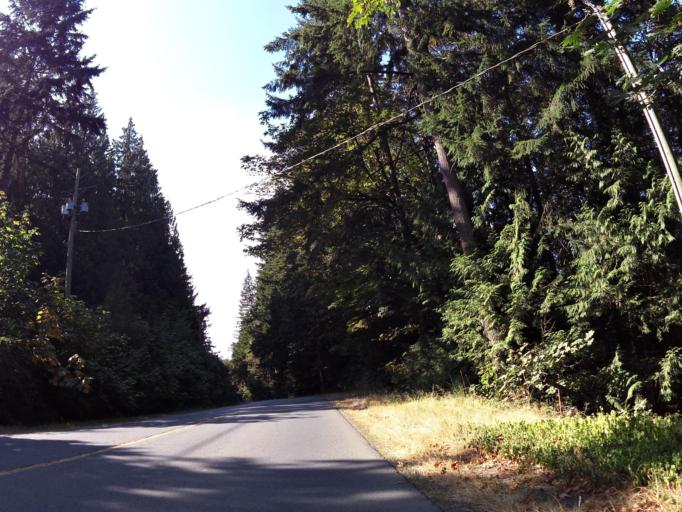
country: CA
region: British Columbia
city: North Saanich
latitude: 48.6925
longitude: -123.5619
